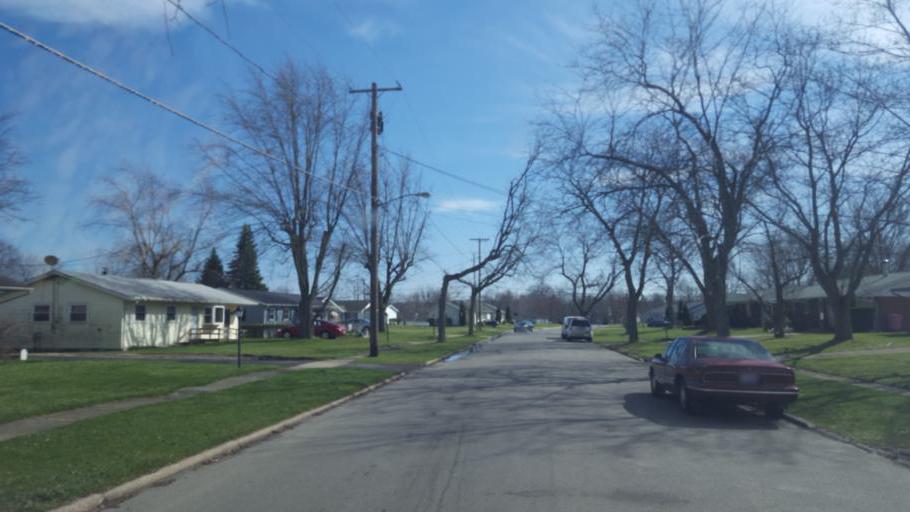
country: US
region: Ohio
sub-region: Richland County
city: Mansfield
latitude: 40.7731
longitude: -82.5476
